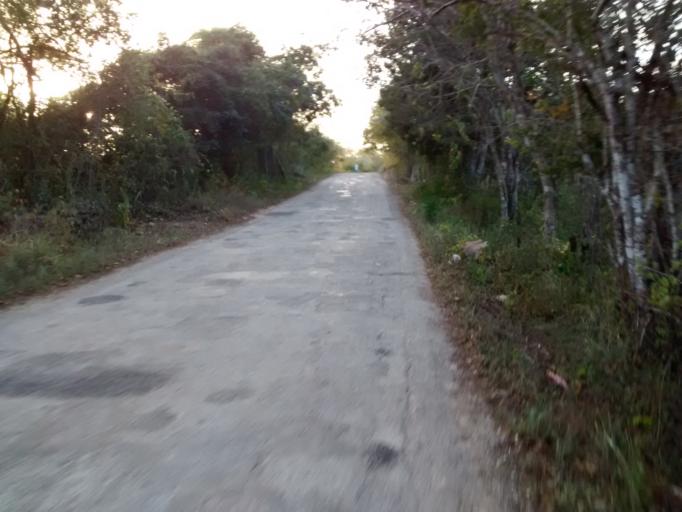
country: MX
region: Yucatan
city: Valladolid
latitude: 20.6823
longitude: -88.1686
